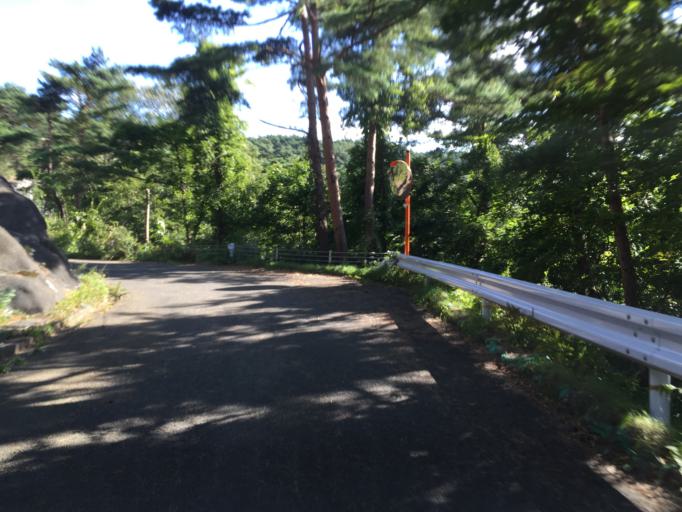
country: JP
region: Fukushima
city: Yanagawamachi-saiwaicho
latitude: 37.8455
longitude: 140.6850
